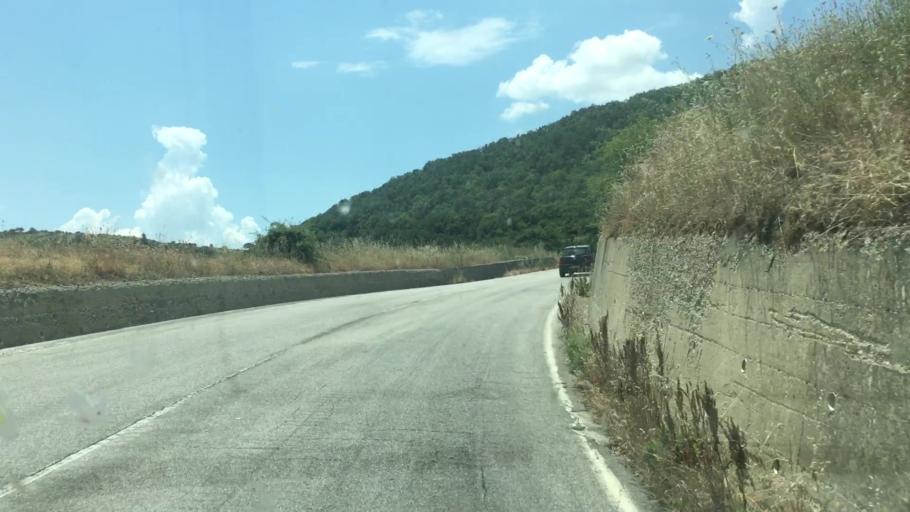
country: IT
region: Basilicate
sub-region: Provincia di Potenza
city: Tolve
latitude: 40.6877
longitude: 15.9842
